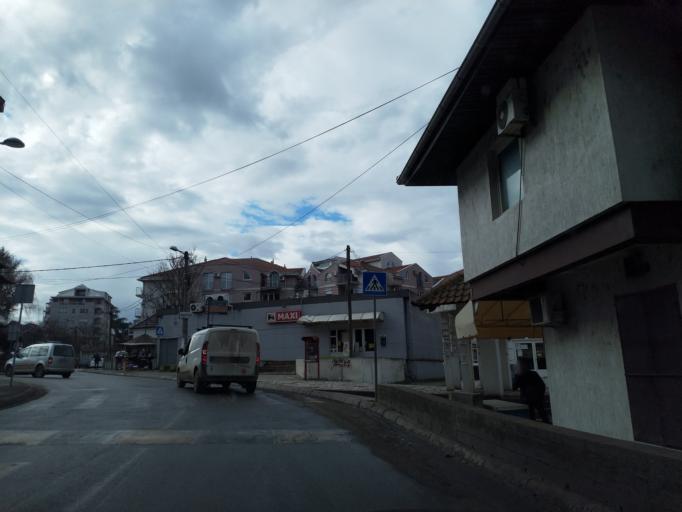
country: RS
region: Central Serbia
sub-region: Belgrade
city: Grocka
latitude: 44.6705
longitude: 20.7175
